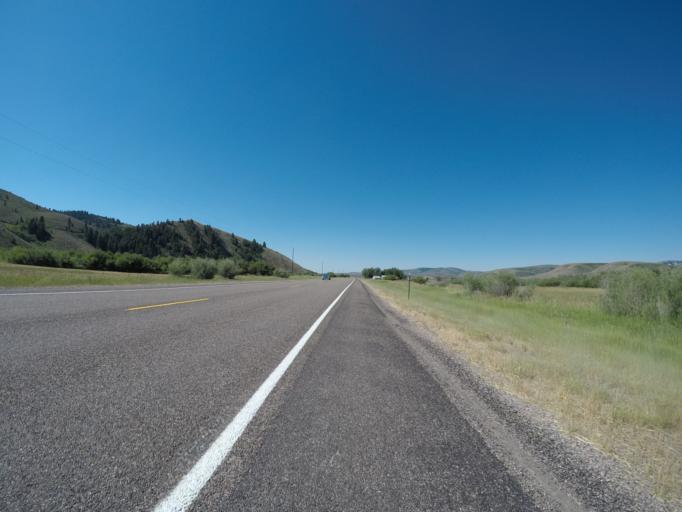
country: US
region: Idaho
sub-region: Bear Lake County
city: Montpelier
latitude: 42.3957
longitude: -111.0502
